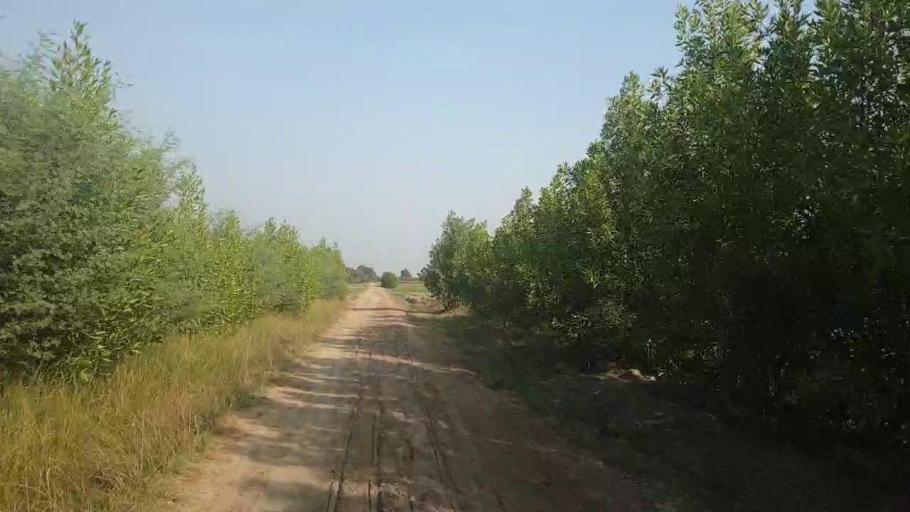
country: PK
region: Sindh
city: Tando Jam
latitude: 25.4295
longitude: 68.4751
